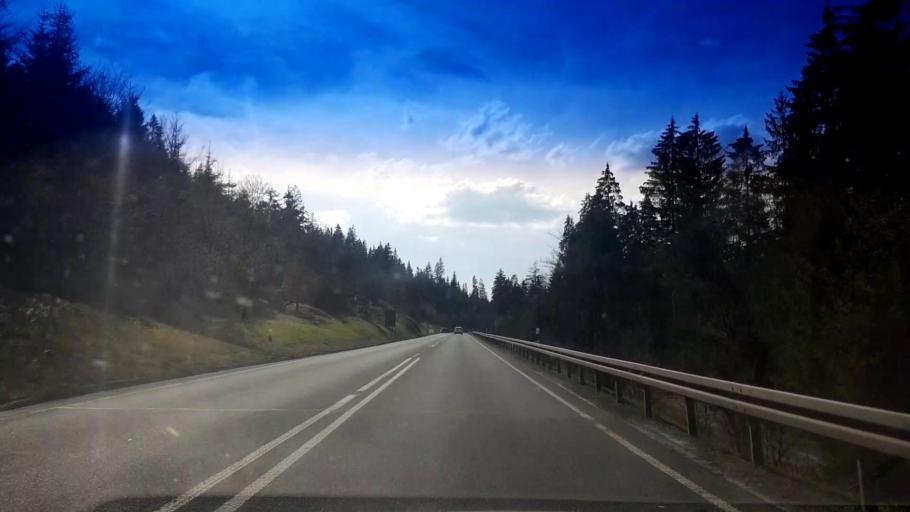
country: DE
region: Bavaria
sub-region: Upper Franconia
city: Bischofsgrun
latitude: 50.0485
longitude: 11.7659
